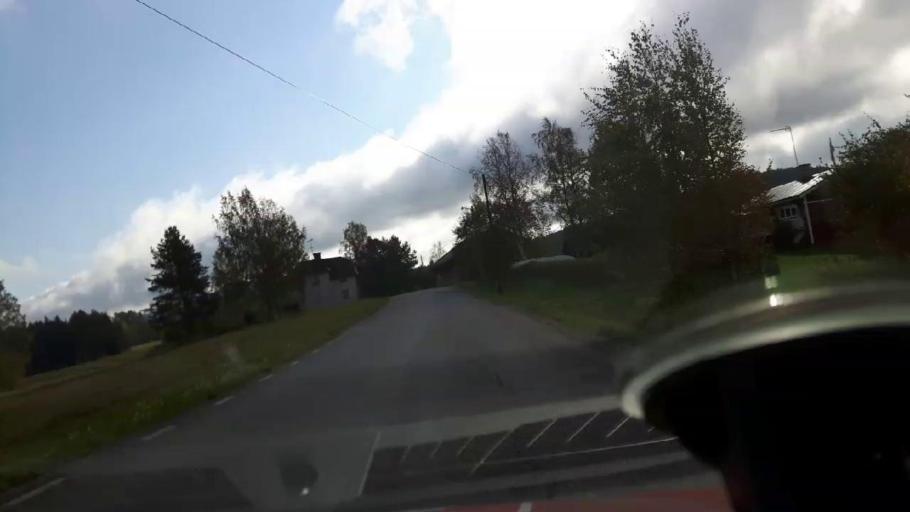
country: SE
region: Gaevleborg
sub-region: Ljusdals Kommun
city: Farila
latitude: 61.7713
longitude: 15.9655
